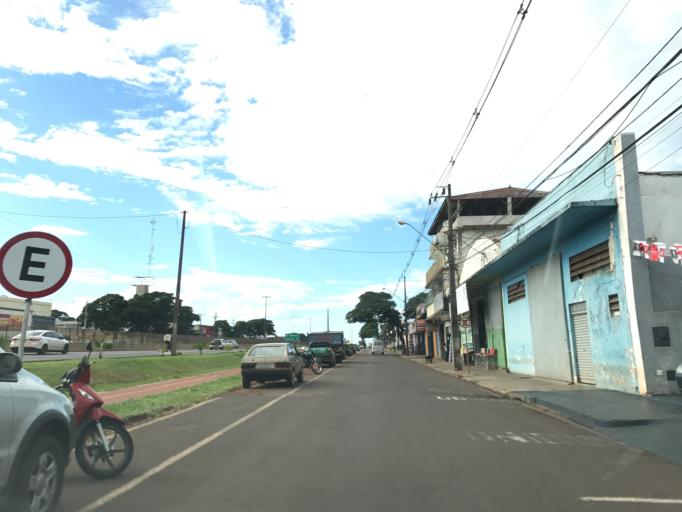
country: BR
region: Parana
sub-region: Sarandi
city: Sarandi
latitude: -23.4370
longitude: -51.8792
